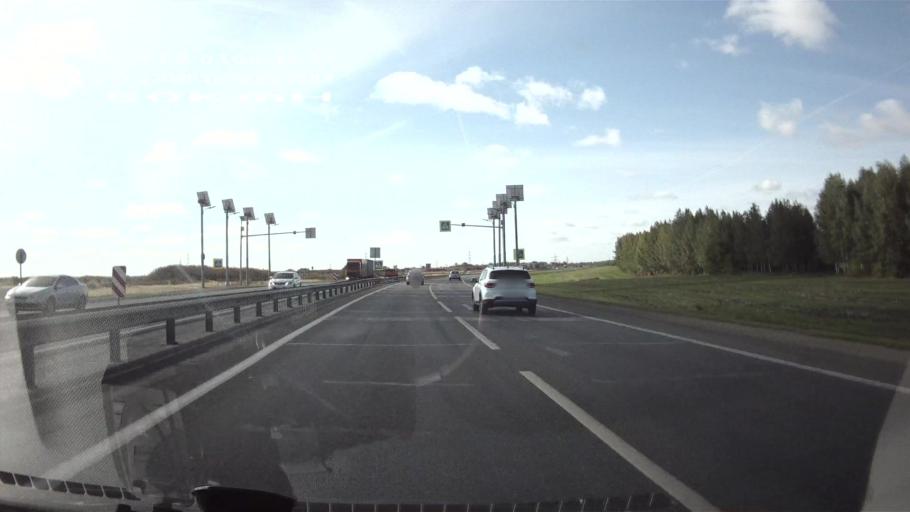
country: RU
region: Ulyanovsk
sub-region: Ulyanovskiy Rayon
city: Ulyanovsk
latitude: 54.2701
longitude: 48.2606
